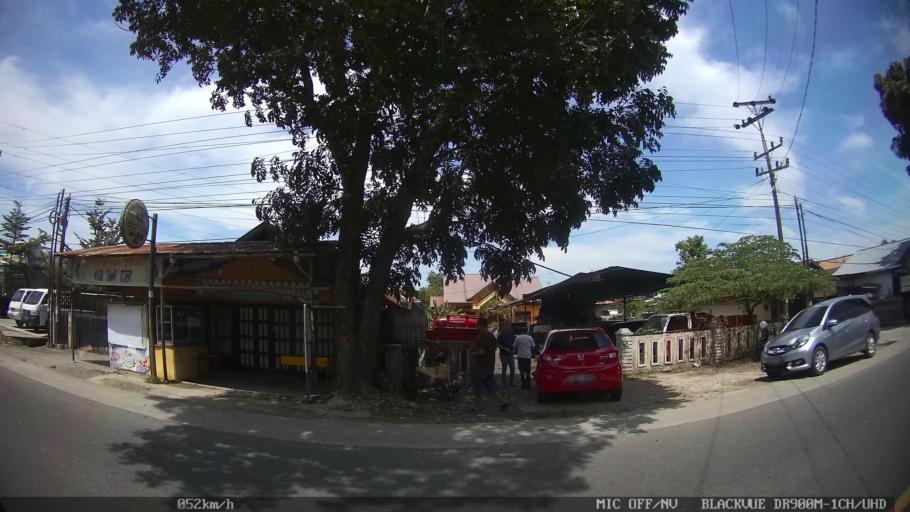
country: ID
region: North Sumatra
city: Binjai
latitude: 3.6447
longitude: 98.5102
